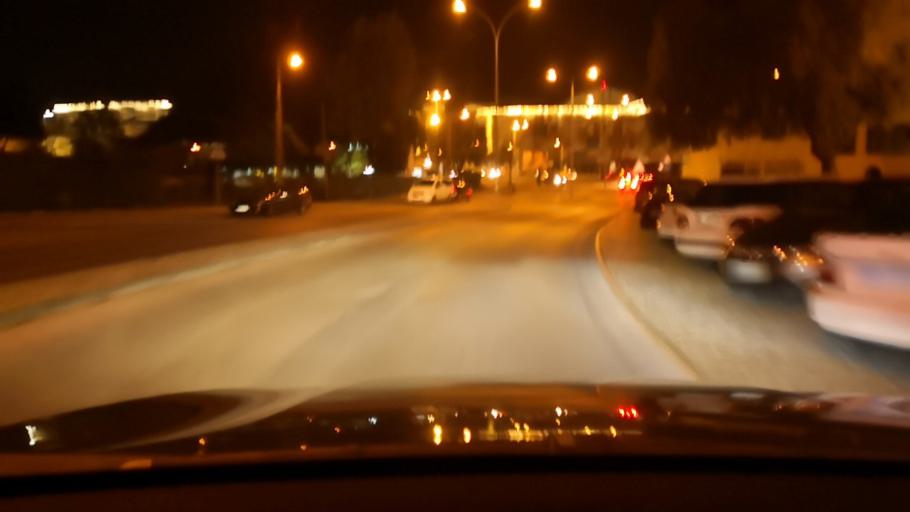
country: PT
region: Setubal
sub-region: Setubal
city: Setubal
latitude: 38.5397
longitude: -8.8767
